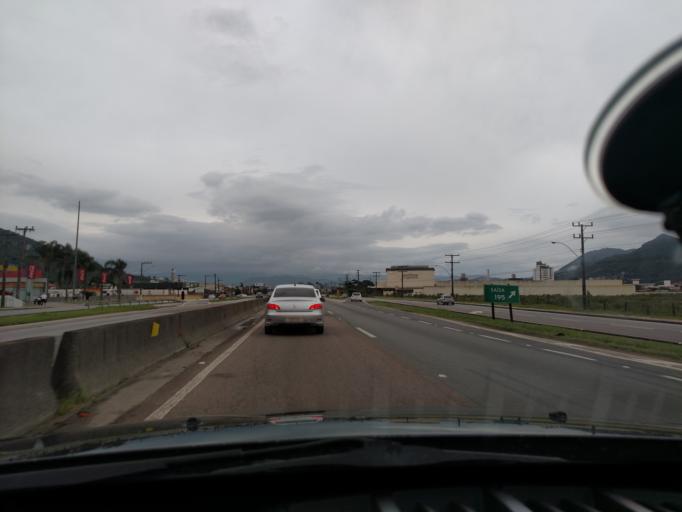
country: BR
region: Santa Catarina
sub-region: Biguacu
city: Biguacu
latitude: -27.5062
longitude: -48.6484
